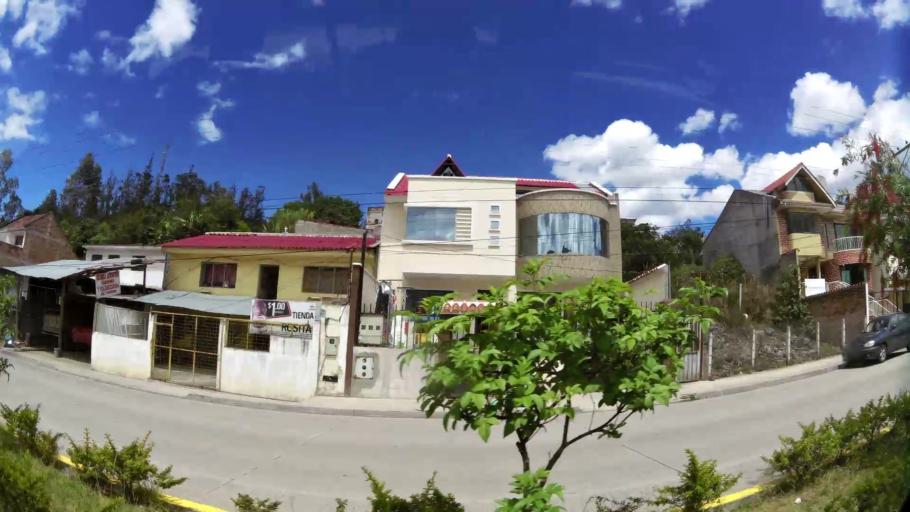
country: EC
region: Azuay
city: Cuenca
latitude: -3.1606
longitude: -79.1510
